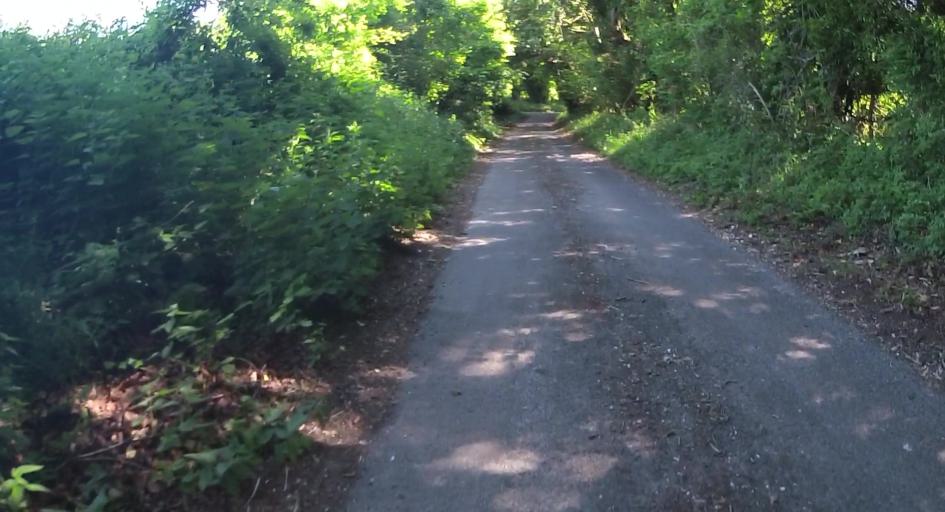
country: GB
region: England
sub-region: Hampshire
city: Old Basing
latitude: 51.2255
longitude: -1.0250
